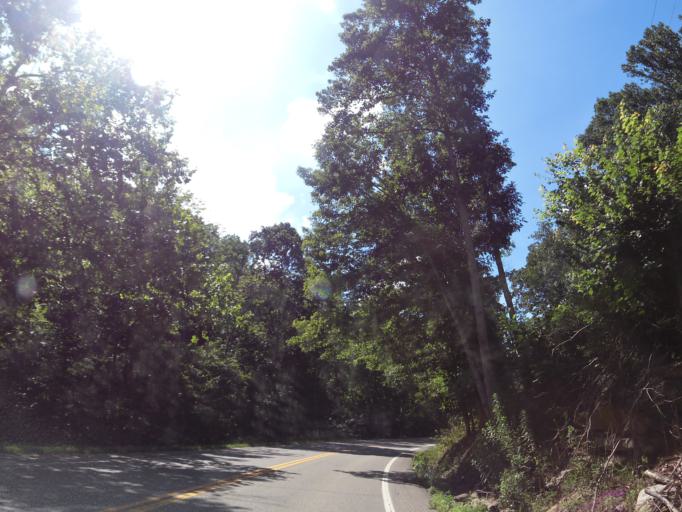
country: US
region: Tennessee
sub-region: Cumberland County
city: Fairfield Glade
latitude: 35.8859
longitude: -84.8356
